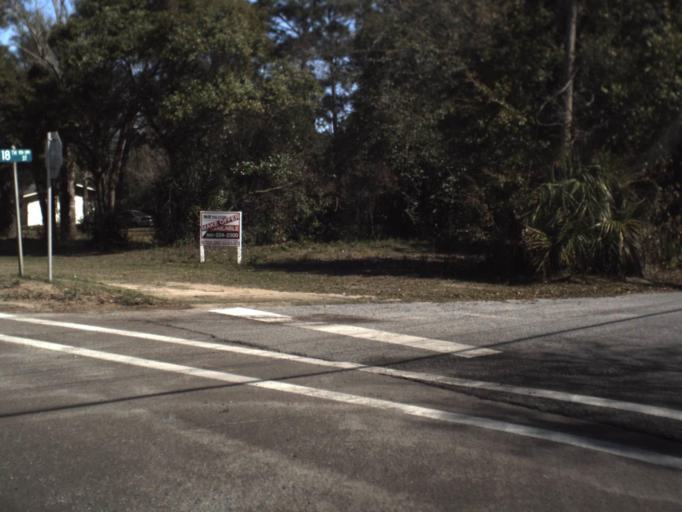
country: US
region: Florida
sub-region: Bay County
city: Lynn Haven
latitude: 30.2320
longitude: -85.6489
